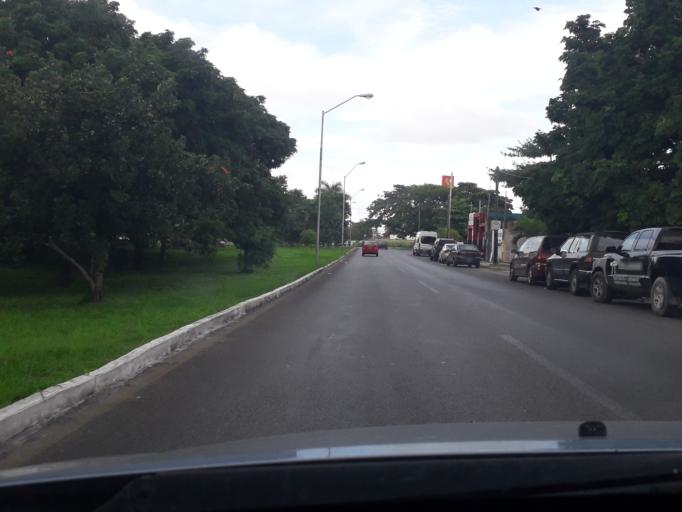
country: MX
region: Yucatan
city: Merida
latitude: 20.9867
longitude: -89.6636
